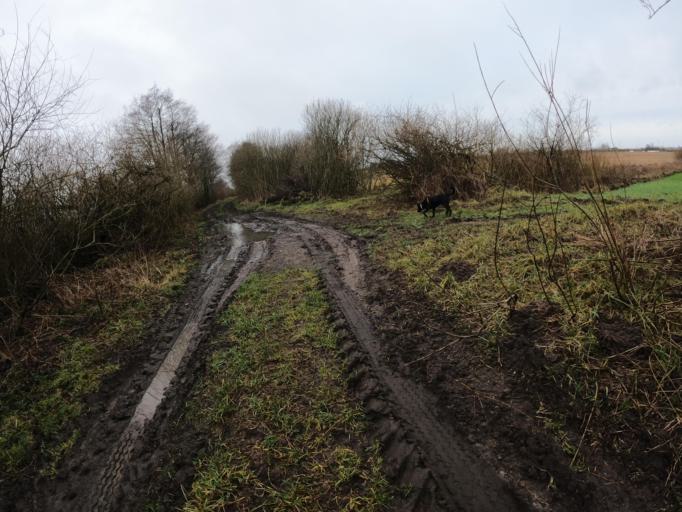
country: PL
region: West Pomeranian Voivodeship
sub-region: Powiat slawienski
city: Darlowo
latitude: 54.4130
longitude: 16.4534
